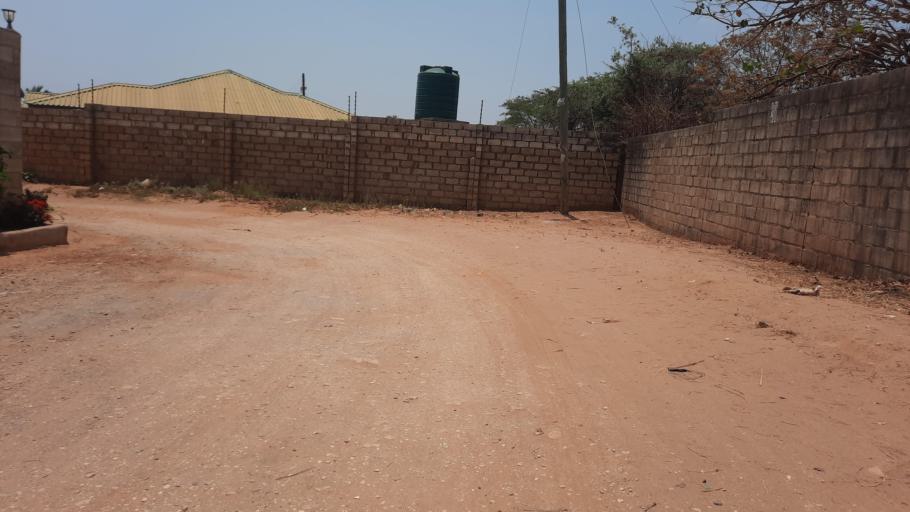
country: ZM
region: Lusaka
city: Lusaka
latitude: -15.4075
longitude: 28.3827
